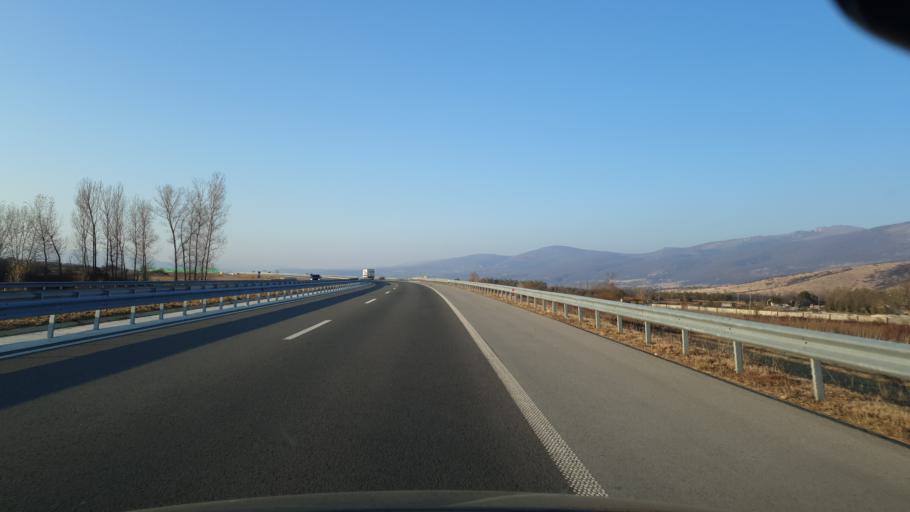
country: RS
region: Central Serbia
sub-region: Pirotski Okrug
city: Dimitrovgrad
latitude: 43.0672
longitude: 22.6789
